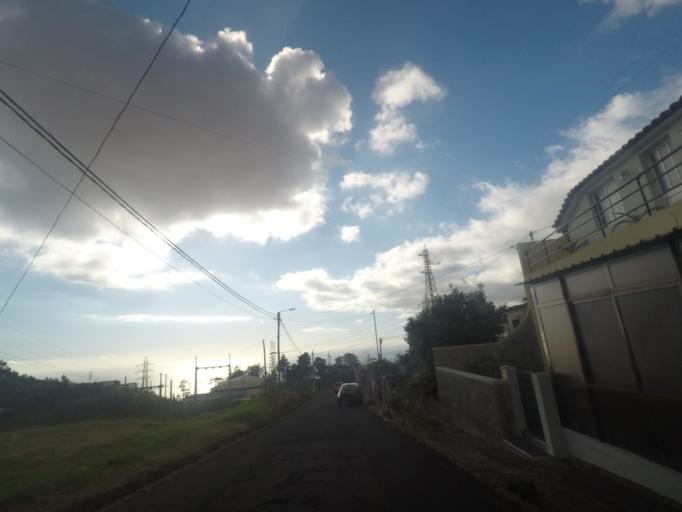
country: PT
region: Madeira
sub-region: Funchal
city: Nossa Senhora do Monte
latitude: 32.6620
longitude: -16.8715
